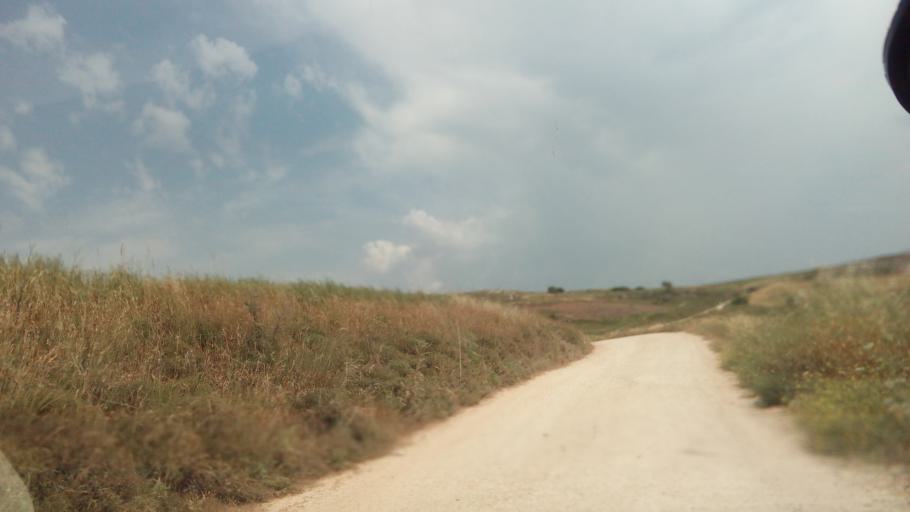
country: CY
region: Pafos
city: Polis
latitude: 34.9756
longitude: 32.3678
